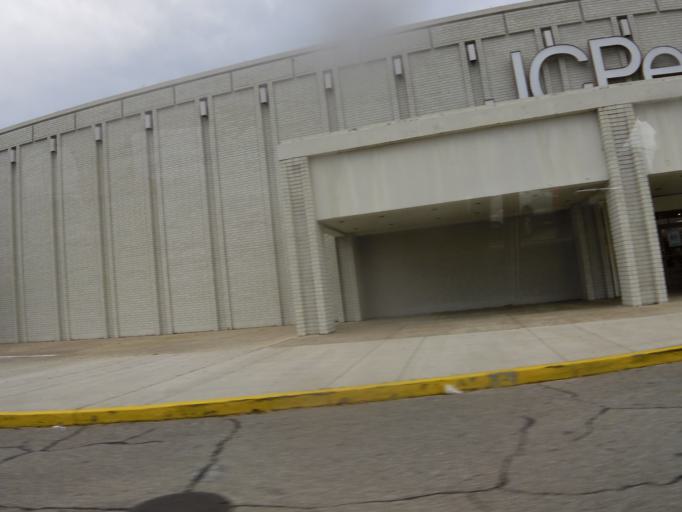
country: US
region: Florida
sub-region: Duval County
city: Jacksonville
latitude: 30.3229
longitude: -81.5488
